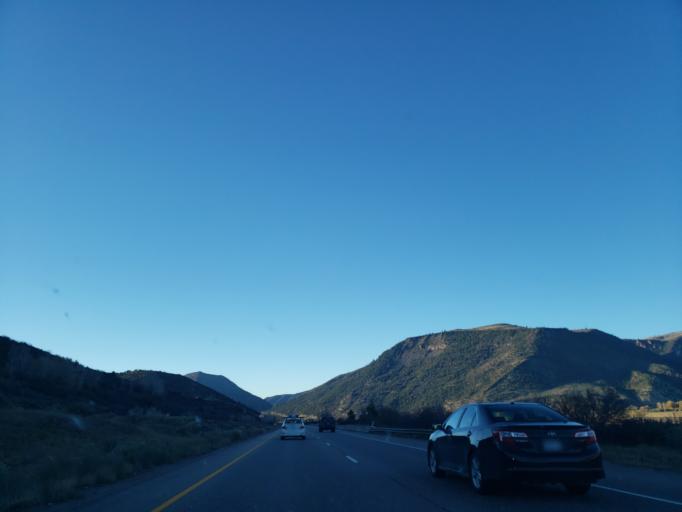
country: US
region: Colorado
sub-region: Pitkin County
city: Snowmass Village
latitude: 39.2777
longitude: -106.8956
